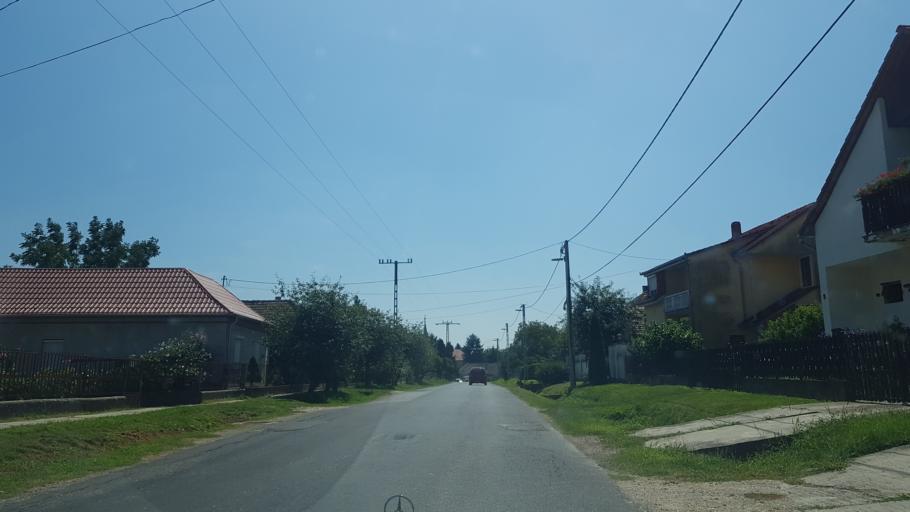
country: HU
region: Somogy
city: Segesd
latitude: 46.3368
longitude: 17.3410
